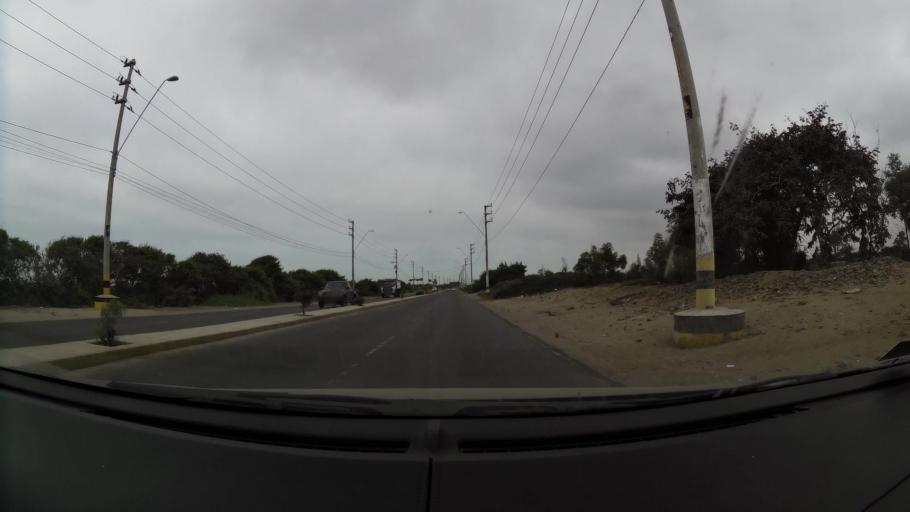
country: PE
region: La Libertad
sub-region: Provincia de Trujillo
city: La Esperanza
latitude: -8.0928
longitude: -79.0780
